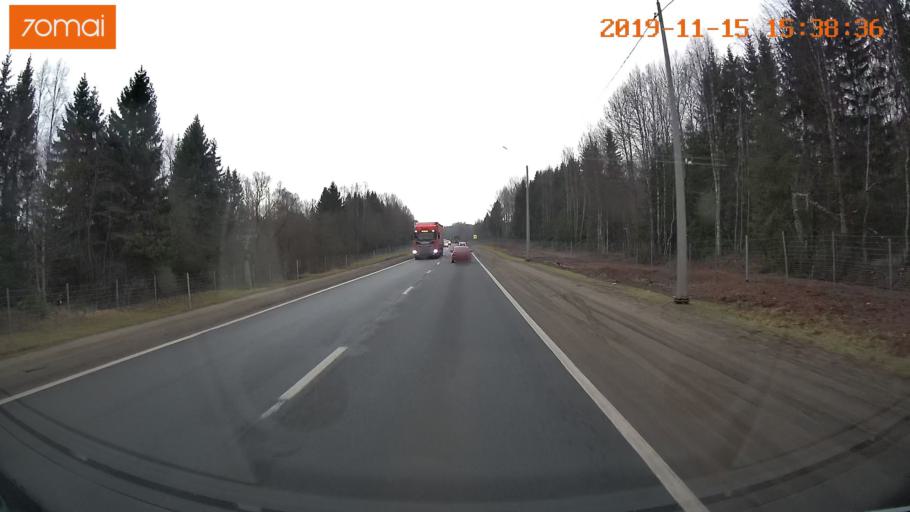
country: RU
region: Jaroslavl
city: Danilov
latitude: 58.0286
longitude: 40.0787
